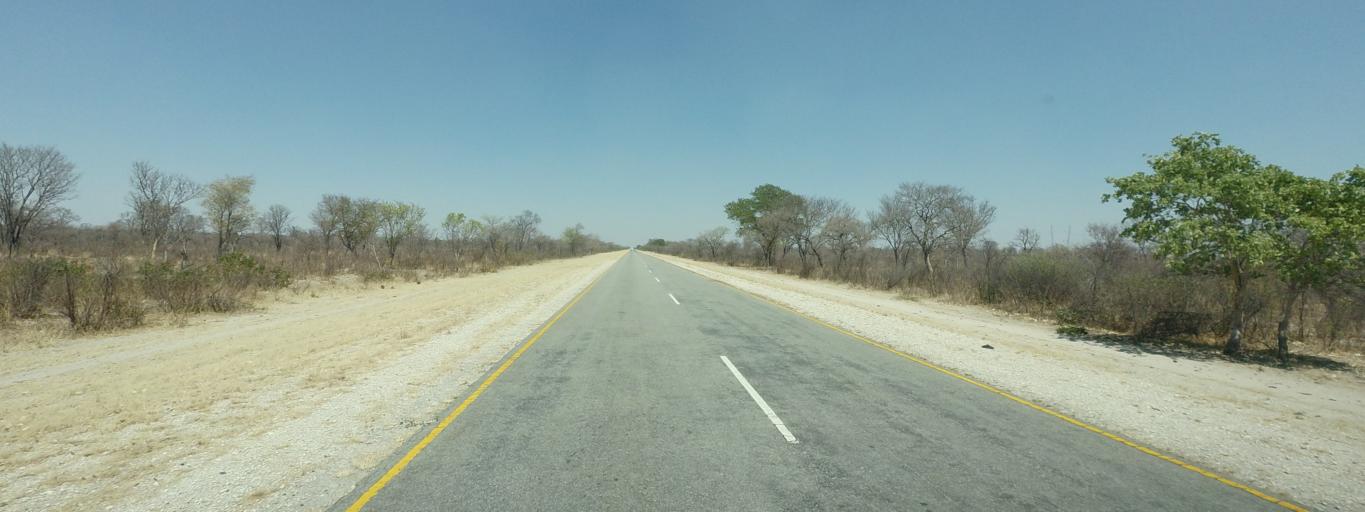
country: BW
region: North West
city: Shakawe
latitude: -18.0489
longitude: 22.1590
